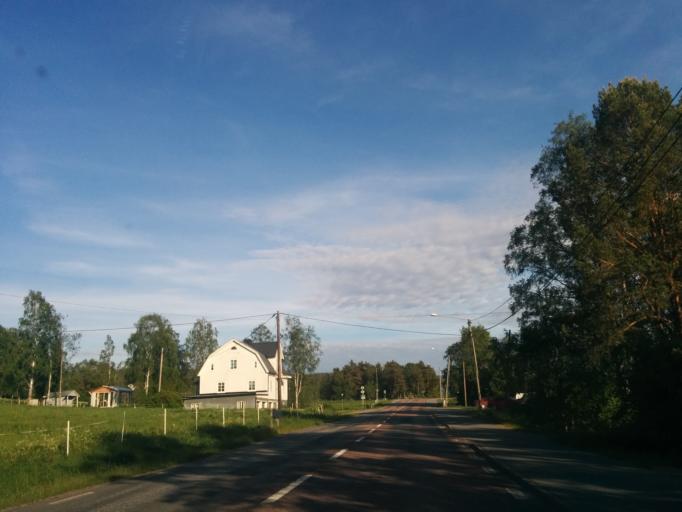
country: SE
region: Vaesternorrland
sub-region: Kramfors Kommun
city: Kramfors
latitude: 62.9695
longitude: 17.8912
